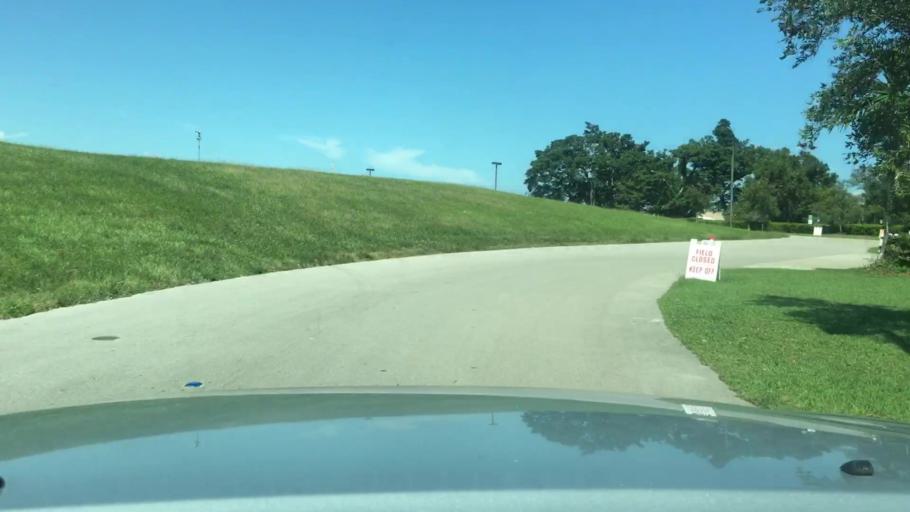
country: US
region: Florida
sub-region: Miami-Dade County
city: Ives Estates
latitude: 25.9714
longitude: -80.1685
